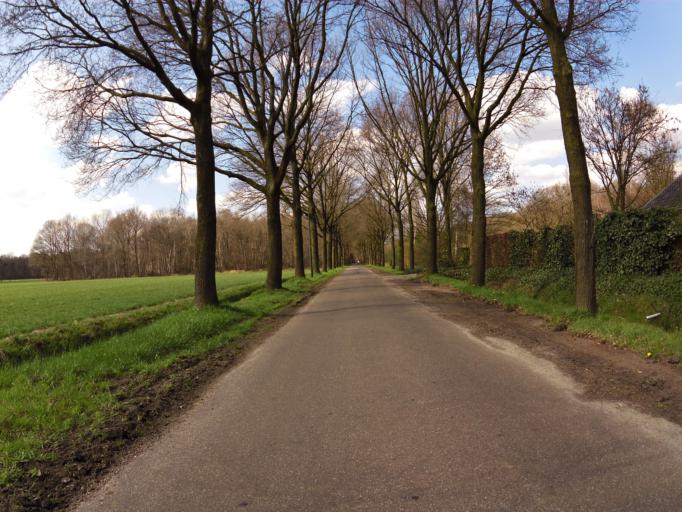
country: NL
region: North Brabant
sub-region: Gemeente Oisterwijk
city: Oisterwijk
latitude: 51.6291
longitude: 5.1771
